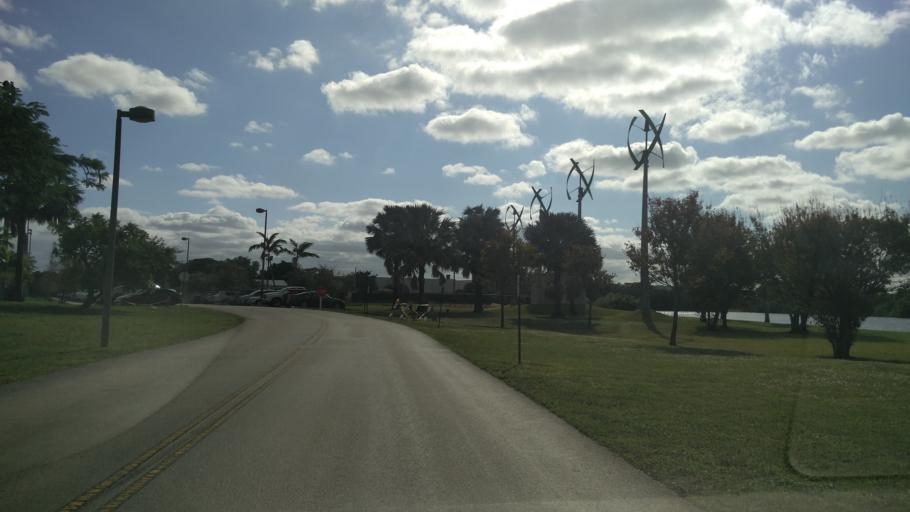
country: US
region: Florida
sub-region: Broward County
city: Rock Island
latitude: 26.1556
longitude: -80.1637
